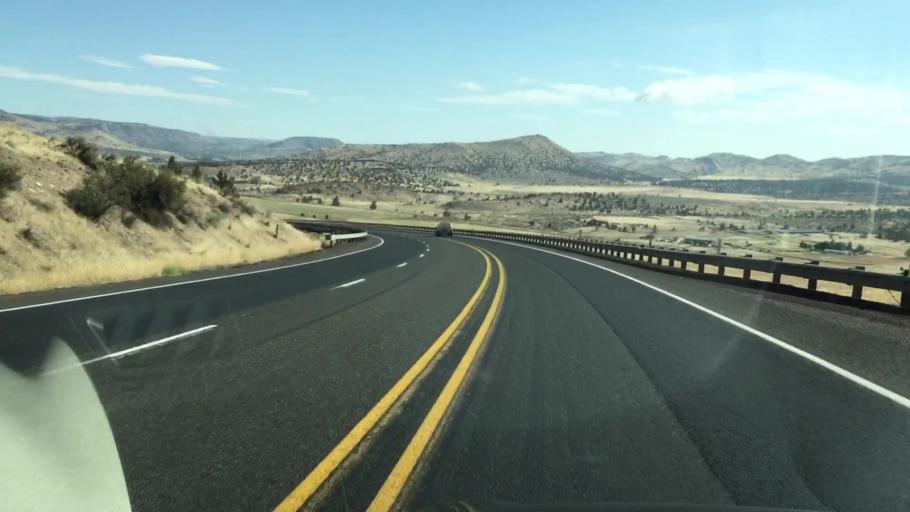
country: US
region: Oregon
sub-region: Jefferson County
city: Madras
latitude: 44.7578
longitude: -120.9762
